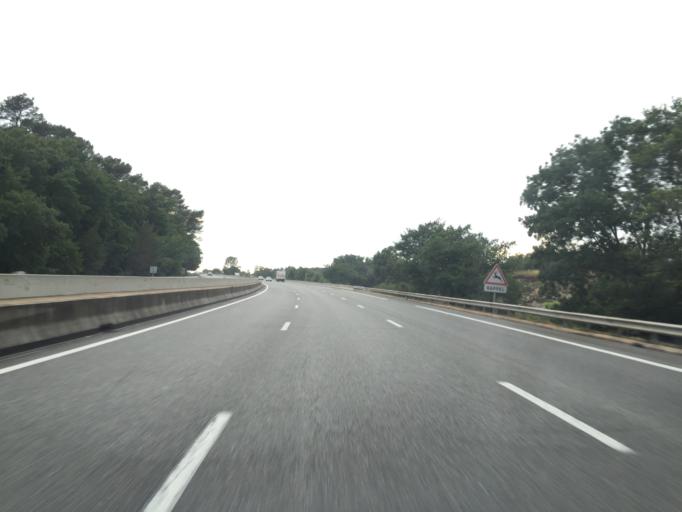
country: FR
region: Provence-Alpes-Cote d'Azur
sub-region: Departement du Var
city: Cabasse
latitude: 43.4101
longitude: 6.1760
